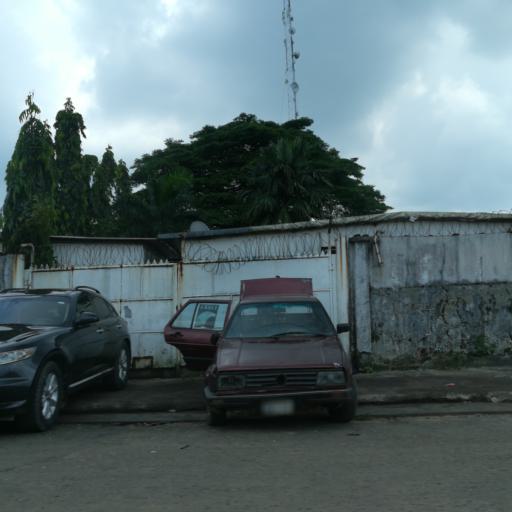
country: NG
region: Rivers
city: Port Harcourt
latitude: 4.8106
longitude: 7.0385
